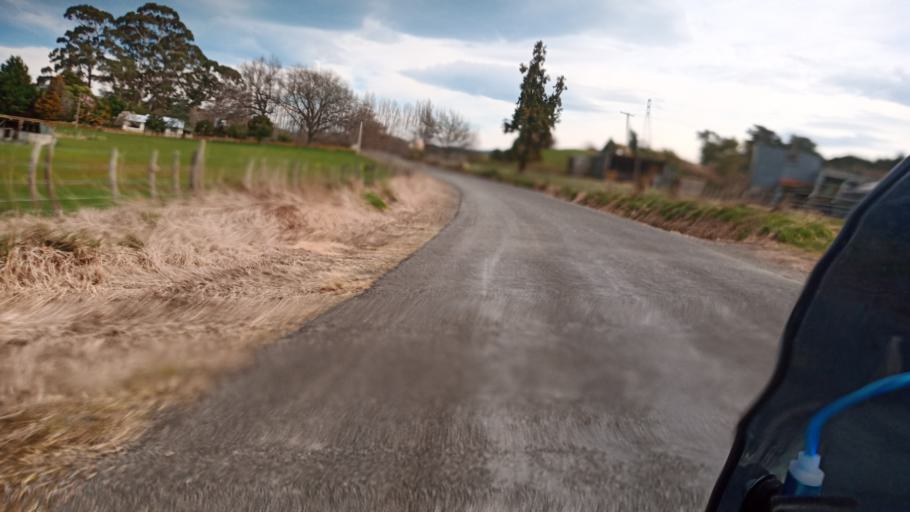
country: NZ
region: Hawke's Bay
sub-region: Wairoa District
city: Wairoa
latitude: -38.9731
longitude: 177.4328
